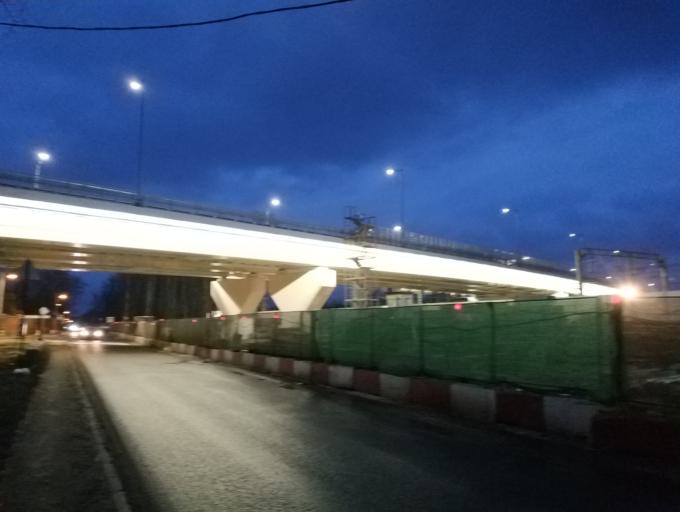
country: RU
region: Moskovskaya
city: Reutov
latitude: 55.7579
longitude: 37.8847
